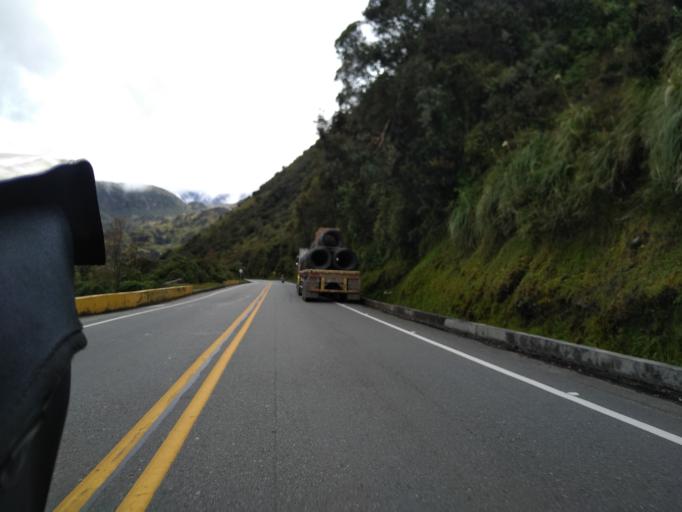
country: CO
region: Tolima
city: Herveo
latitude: 5.0280
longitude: -75.3343
